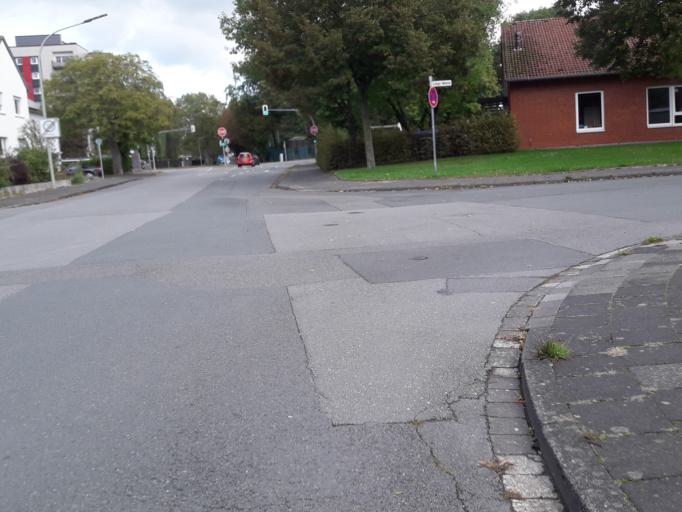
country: DE
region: North Rhine-Westphalia
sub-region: Regierungsbezirk Detmold
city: Paderborn
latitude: 51.7211
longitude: 8.7772
